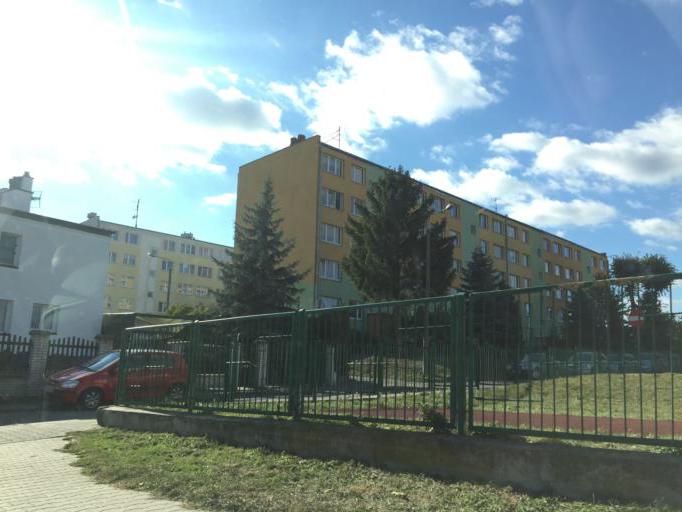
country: PL
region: Warmian-Masurian Voivodeship
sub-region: Powiat bartoszycki
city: Bartoszyce
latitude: 54.2448
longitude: 20.8159
